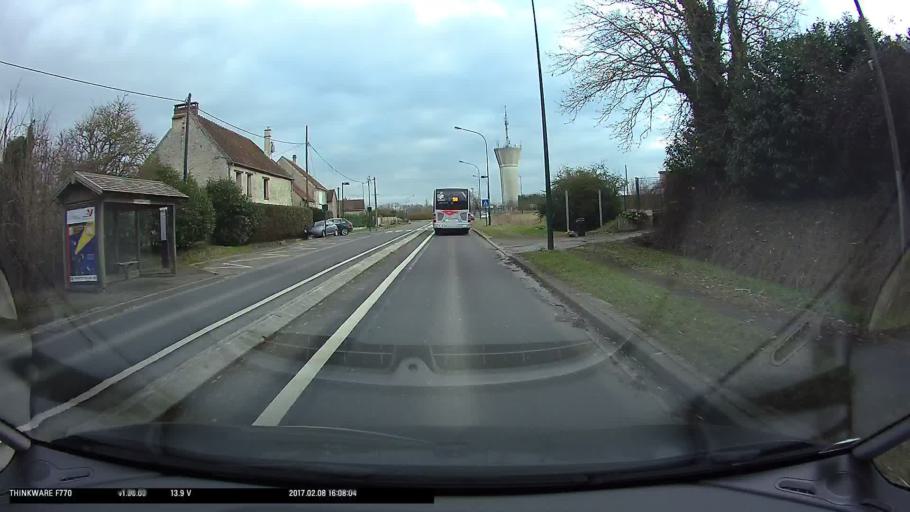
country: FR
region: Ile-de-France
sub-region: Departement du Val-d'Oise
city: Marines
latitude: 49.1260
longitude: 1.9997
